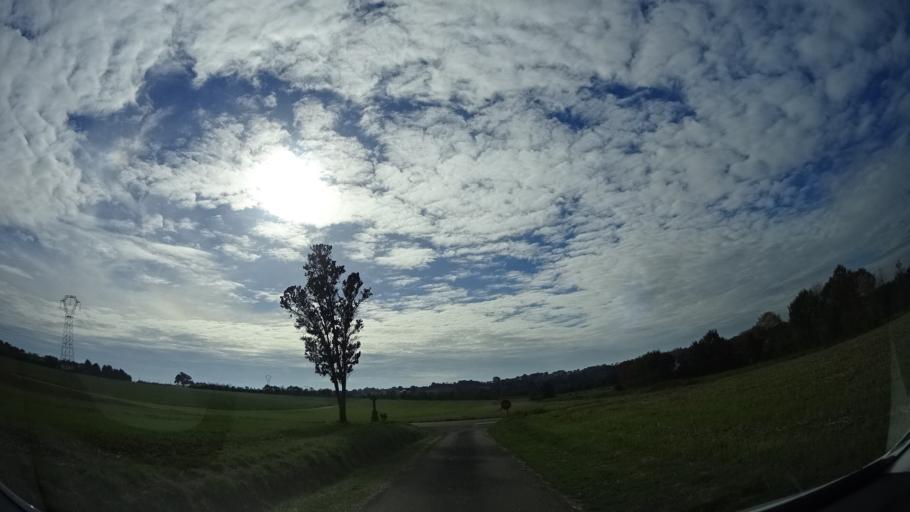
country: FR
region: Brittany
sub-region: Departement d'Ille-et-Vilaine
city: Vignoc
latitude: 48.2436
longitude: -1.8136
